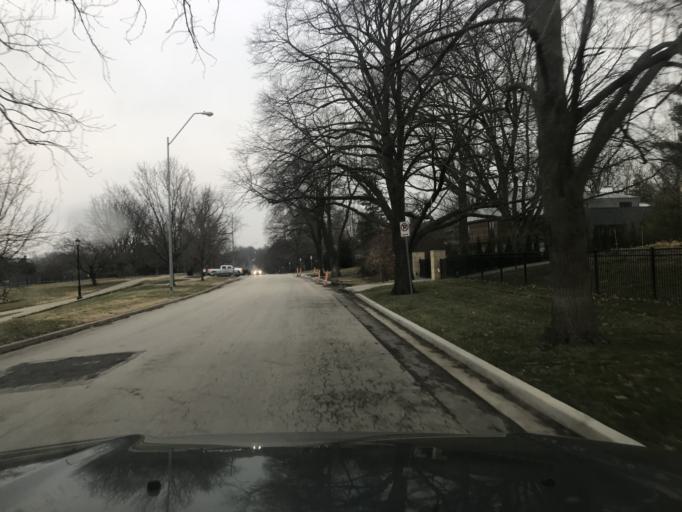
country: US
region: Kansas
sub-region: Johnson County
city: Westwood
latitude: 39.0335
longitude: -94.5968
